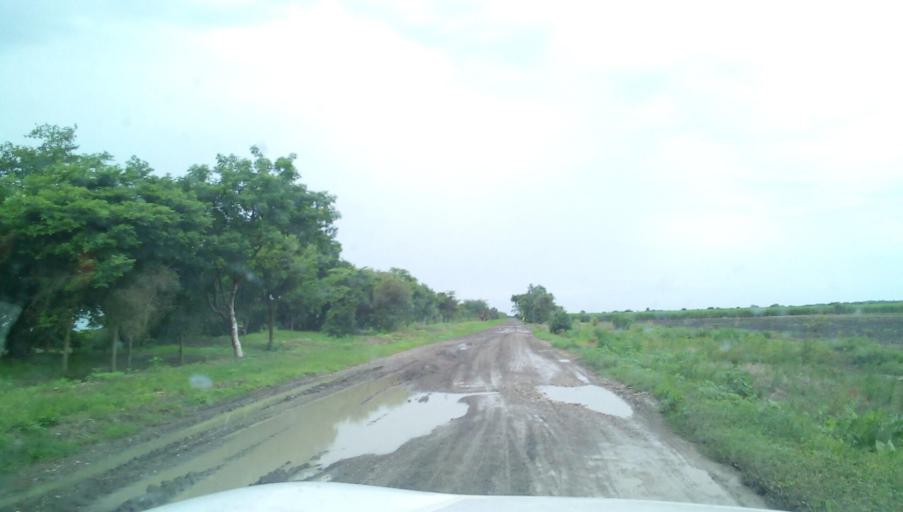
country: MX
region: Veracruz
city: Panuco
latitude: 21.8166
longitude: -98.1110
